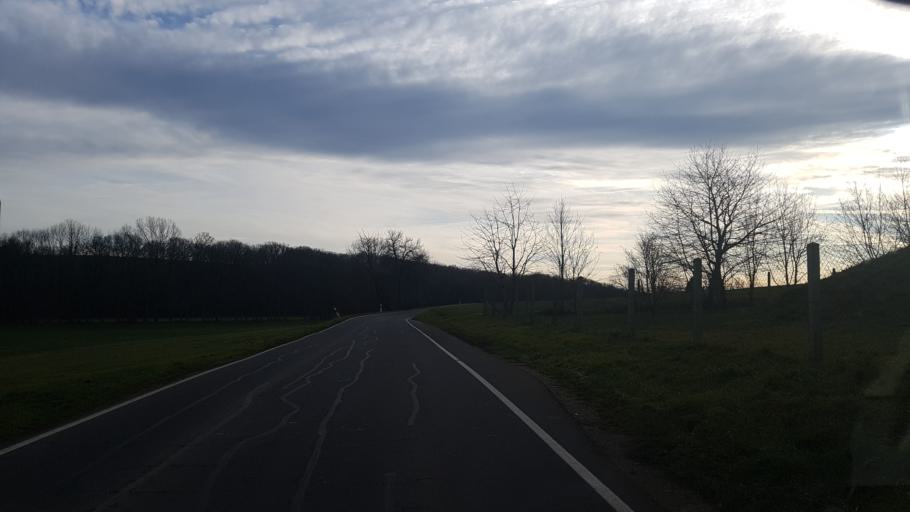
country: DE
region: Saxony
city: Ostrau
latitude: 51.1872
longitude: 13.1665
